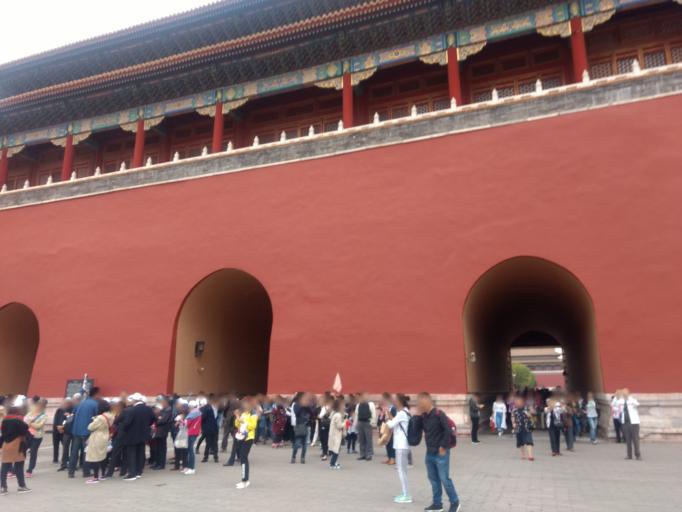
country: CN
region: Beijing
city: Beijing
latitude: 39.9128
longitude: 116.3908
